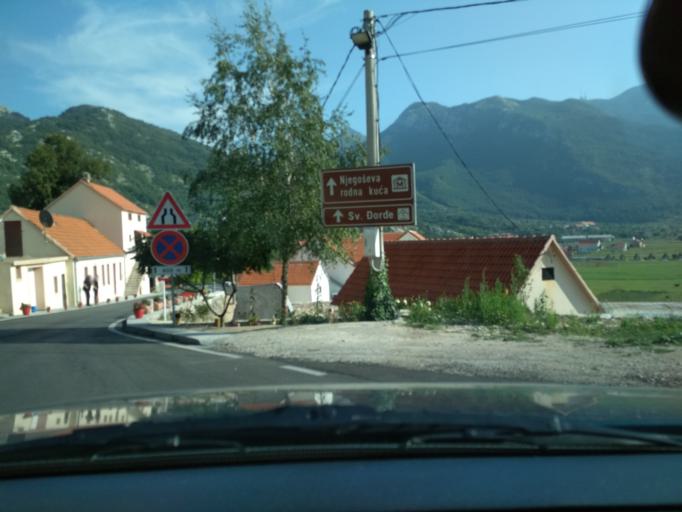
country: ME
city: Dobrota
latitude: 42.4378
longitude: 18.8288
